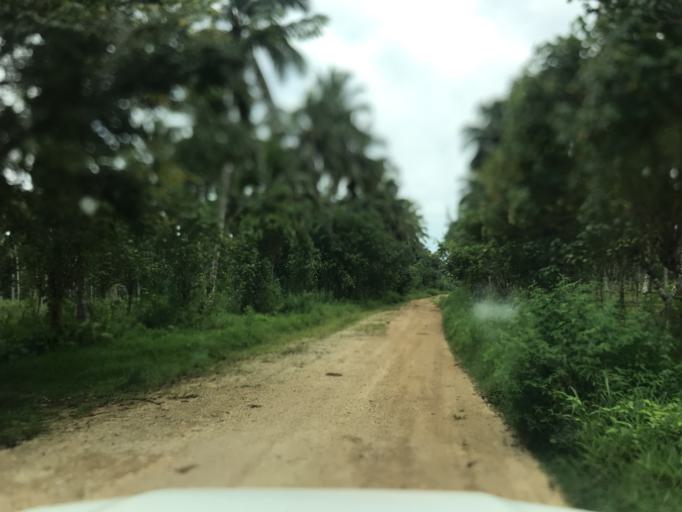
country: VU
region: Sanma
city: Port-Olry
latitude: -15.1874
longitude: 167.0184
